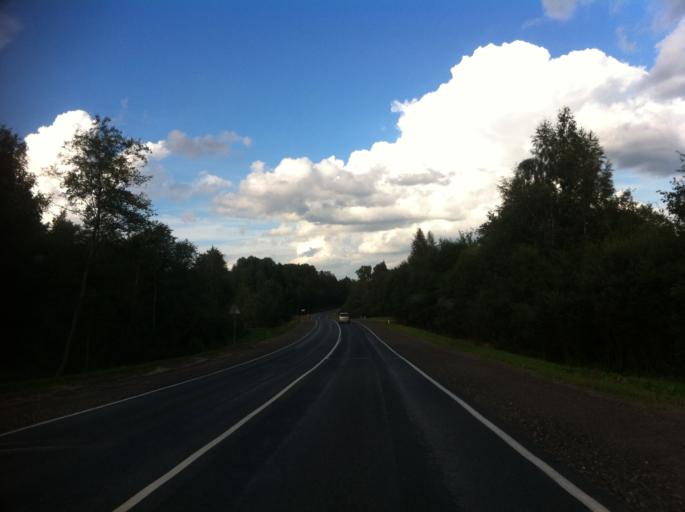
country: RU
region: Pskov
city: Strugi-Krasnyye
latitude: 58.1928
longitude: 29.2809
